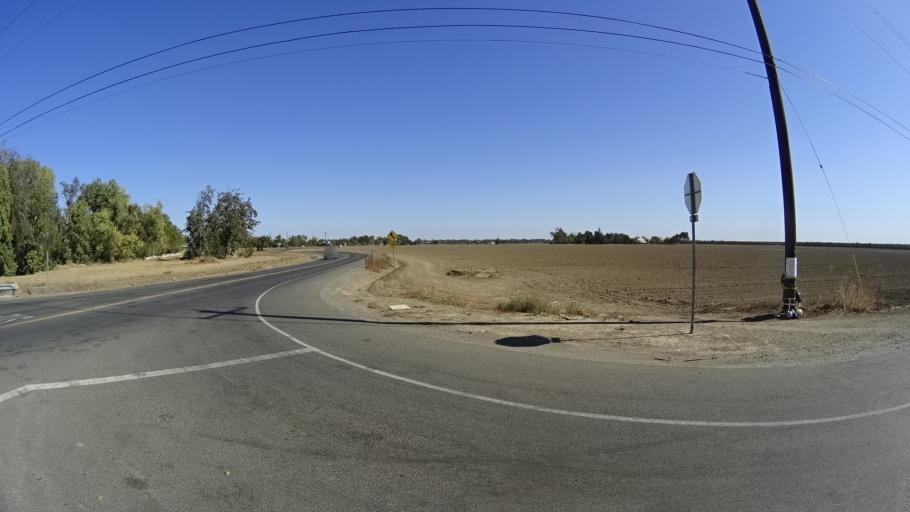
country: US
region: California
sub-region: Yolo County
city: Davis
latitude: 38.5897
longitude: -121.8032
